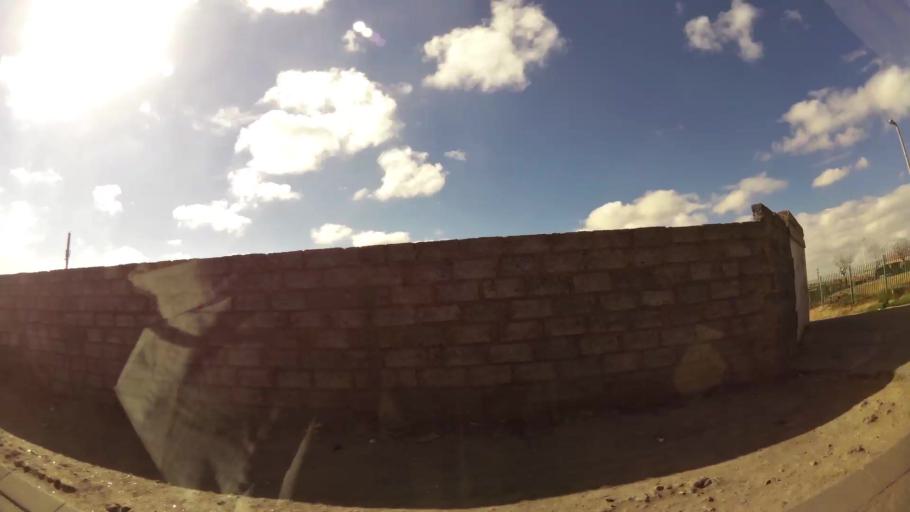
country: ZA
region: Gauteng
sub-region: City of Johannesburg Metropolitan Municipality
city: Modderfontein
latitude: -26.0425
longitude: 28.1810
